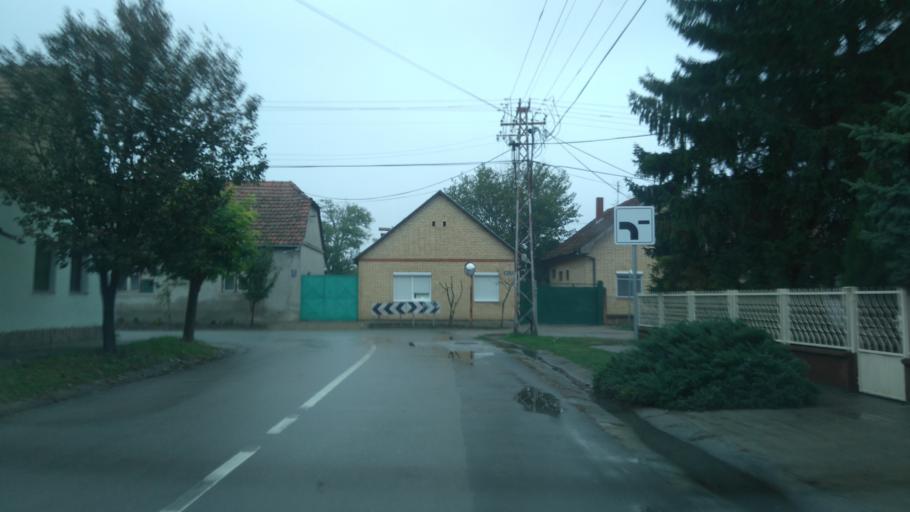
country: RS
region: Autonomna Pokrajina Vojvodina
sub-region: Juznobacki Okrug
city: Becej
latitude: 45.6190
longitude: 20.0603
